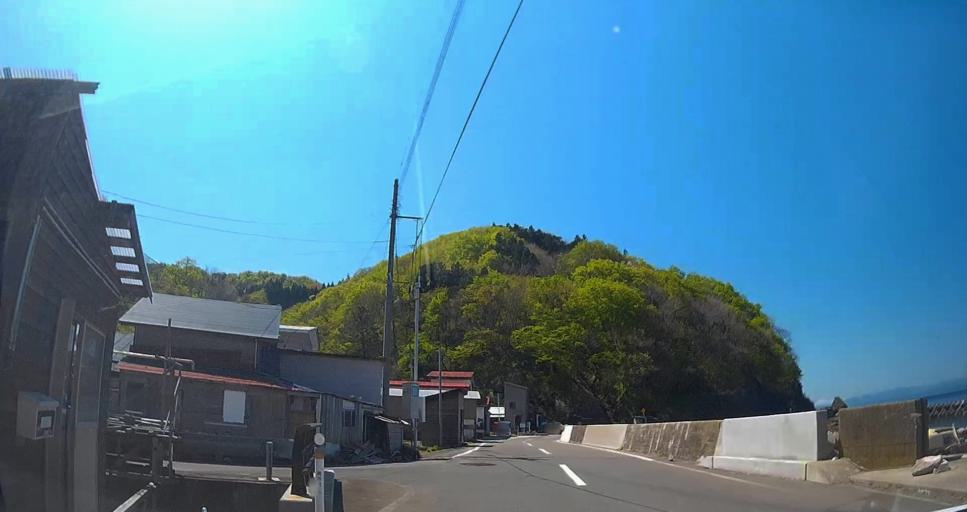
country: JP
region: Aomori
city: Aomori Shi
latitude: 41.1382
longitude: 140.7796
